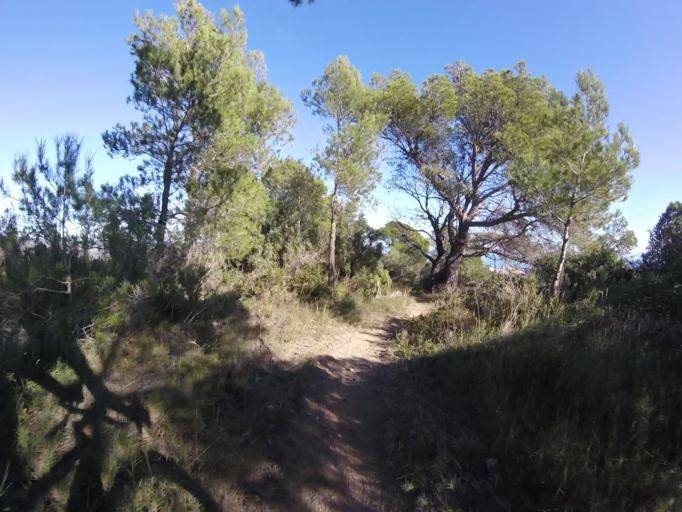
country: ES
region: Valencia
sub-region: Provincia de Castello
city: Orpesa/Oropesa del Mar
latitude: 40.1082
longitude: 0.1186
